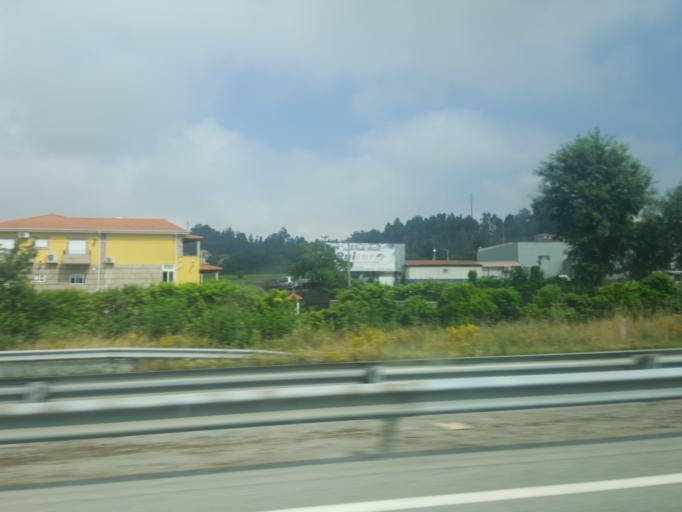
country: PT
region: Porto
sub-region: Lousada
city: Meinedo
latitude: 41.2219
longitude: -8.2375
